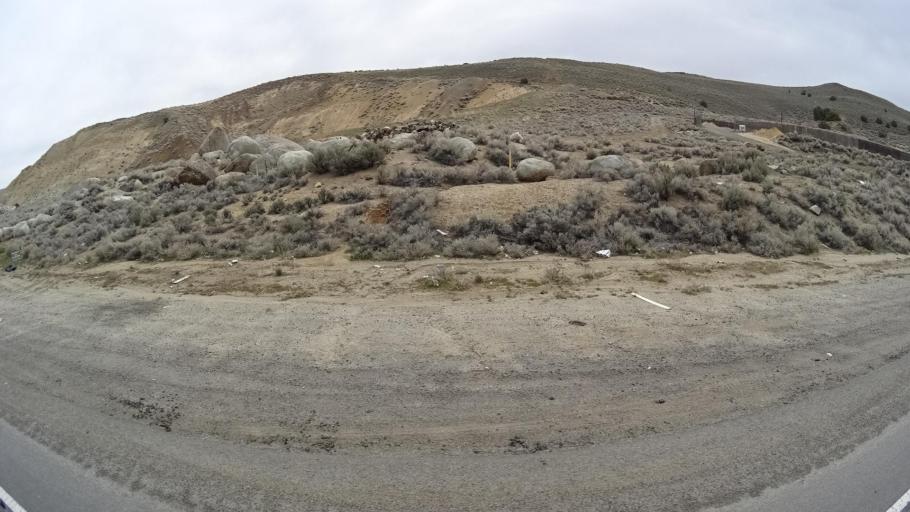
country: US
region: Nevada
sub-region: Washoe County
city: Sun Valley
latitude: 39.6089
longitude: -119.7439
